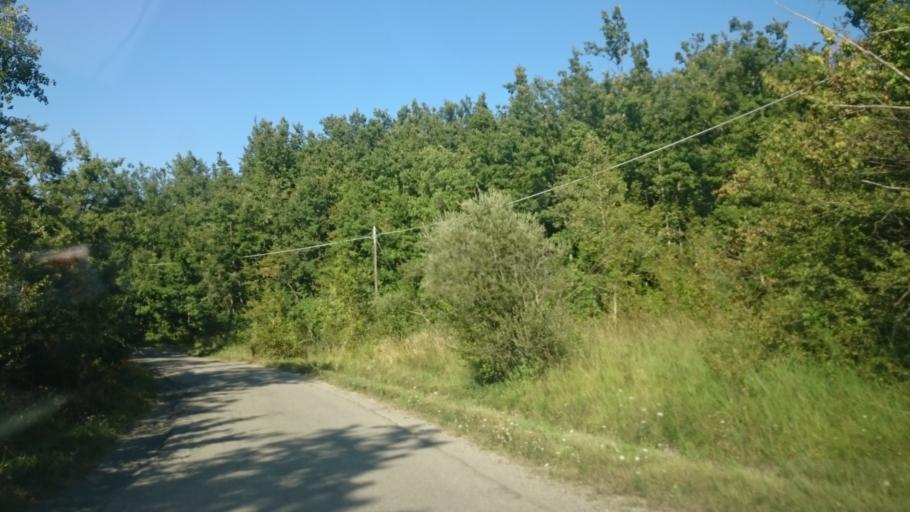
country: IT
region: Emilia-Romagna
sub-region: Provincia di Reggio Emilia
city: Villa Minozzo
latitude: 44.3390
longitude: 10.4789
